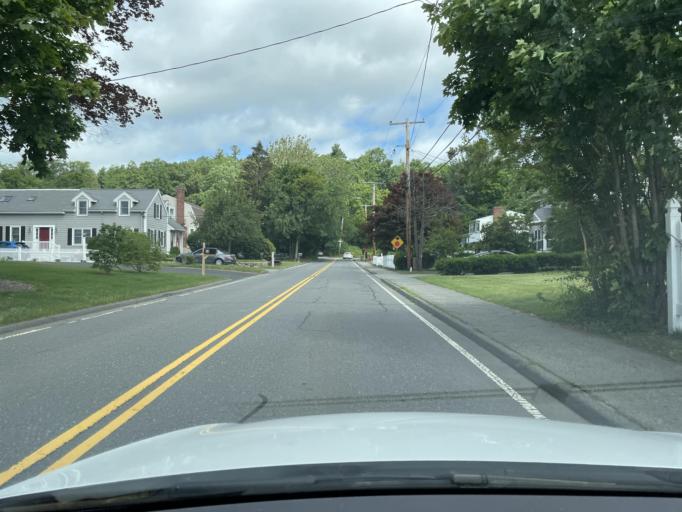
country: US
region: Massachusetts
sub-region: Middlesex County
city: Woburn
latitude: 42.4866
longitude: -71.1757
